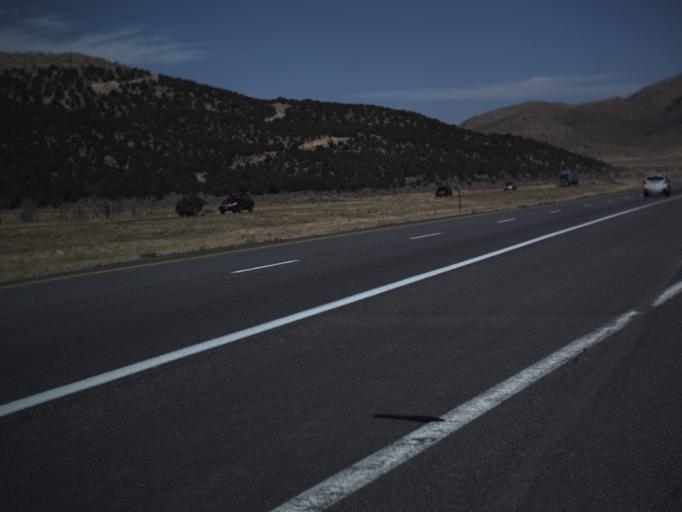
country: US
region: Utah
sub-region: Beaver County
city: Beaver
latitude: 38.6559
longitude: -112.5960
